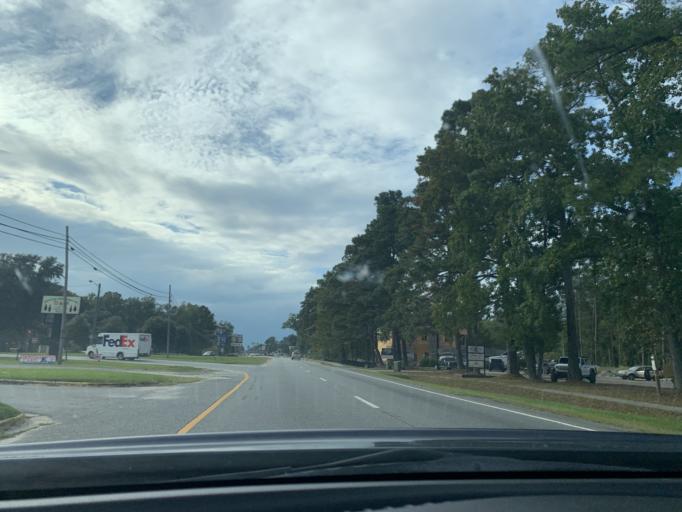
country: US
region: Georgia
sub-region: Chatham County
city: Pooler
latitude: 32.1185
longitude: -81.2557
